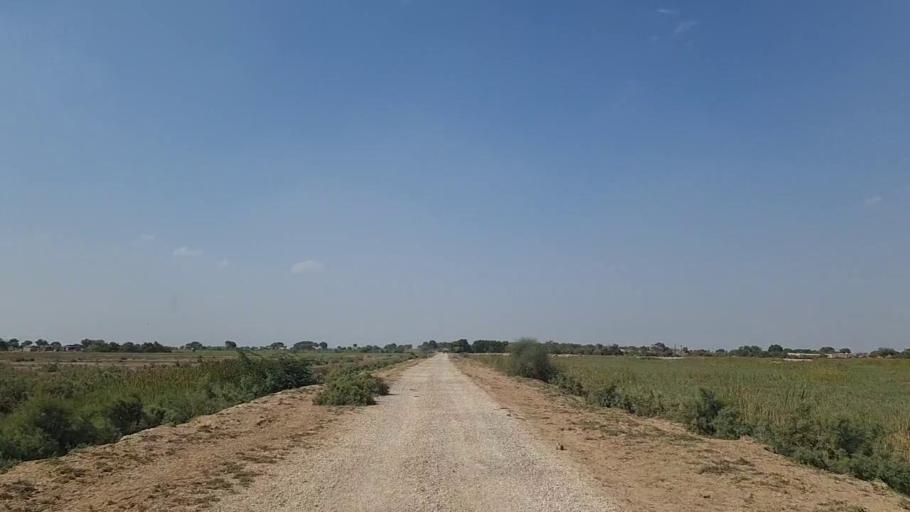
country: PK
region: Sindh
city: Jati
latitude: 24.5153
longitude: 68.2945
